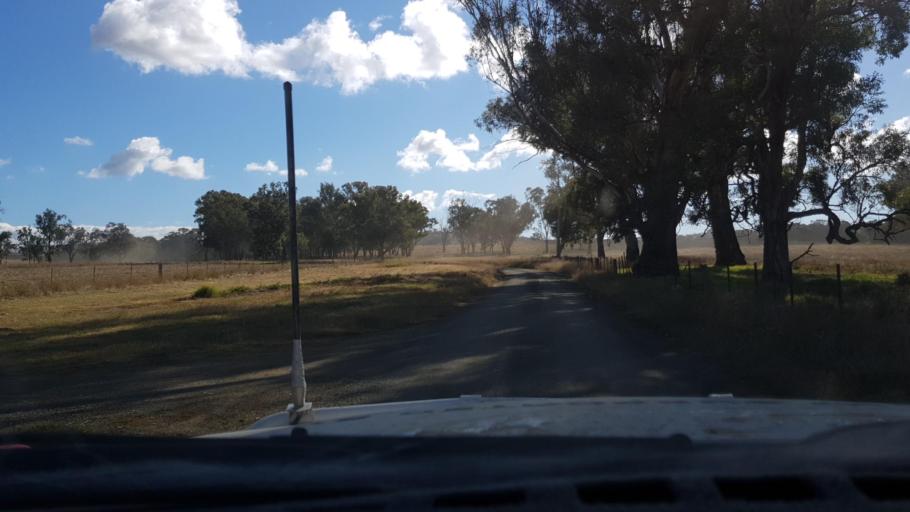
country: AU
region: New South Wales
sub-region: Narrabri
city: Blair Athol
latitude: -30.5712
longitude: 150.4716
